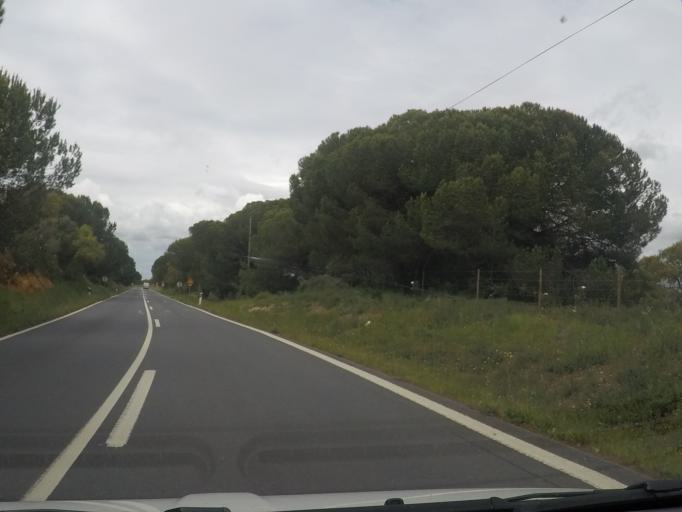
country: PT
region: Setubal
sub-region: Sines
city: Porto Covo
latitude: 37.8762
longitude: -8.7431
